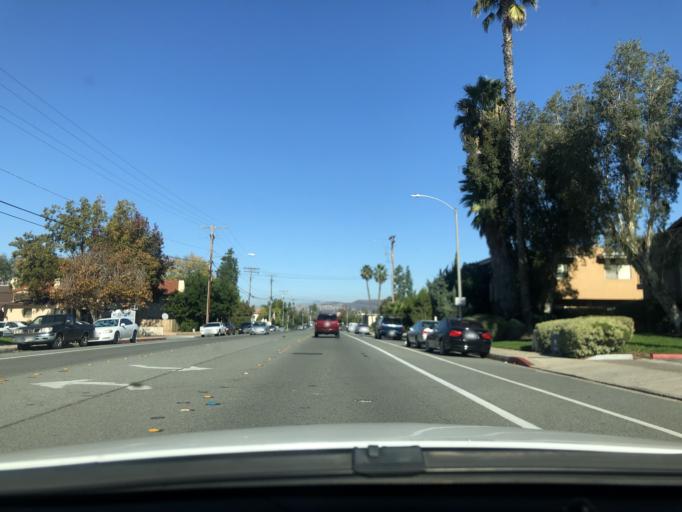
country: US
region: California
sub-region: San Diego County
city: El Cajon
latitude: 32.7826
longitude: -116.9509
